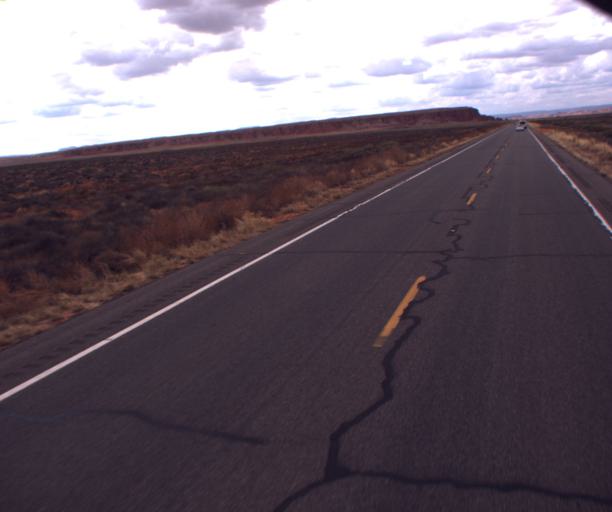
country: US
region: Arizona
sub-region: Navajo County
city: Kayenta
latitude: 36.7830
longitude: -109.9783
